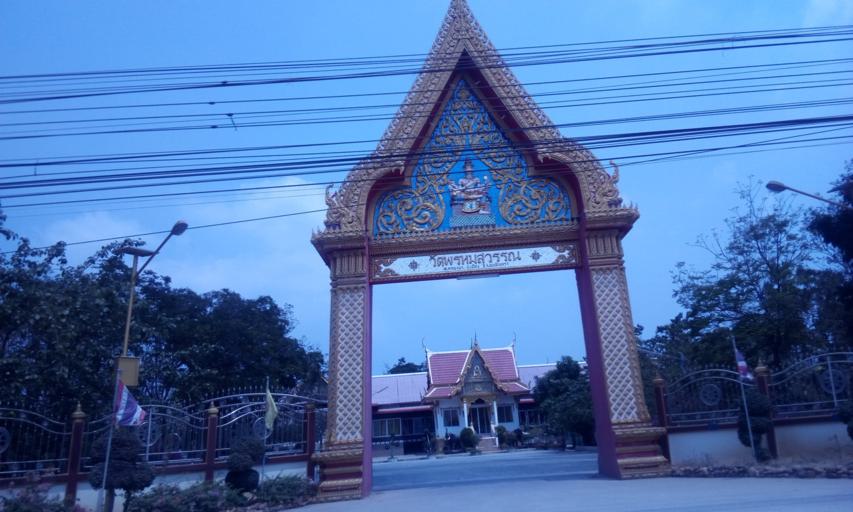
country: TH
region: Chachoengsao
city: Ban Pho
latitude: 13.6449
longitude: 101.1006
